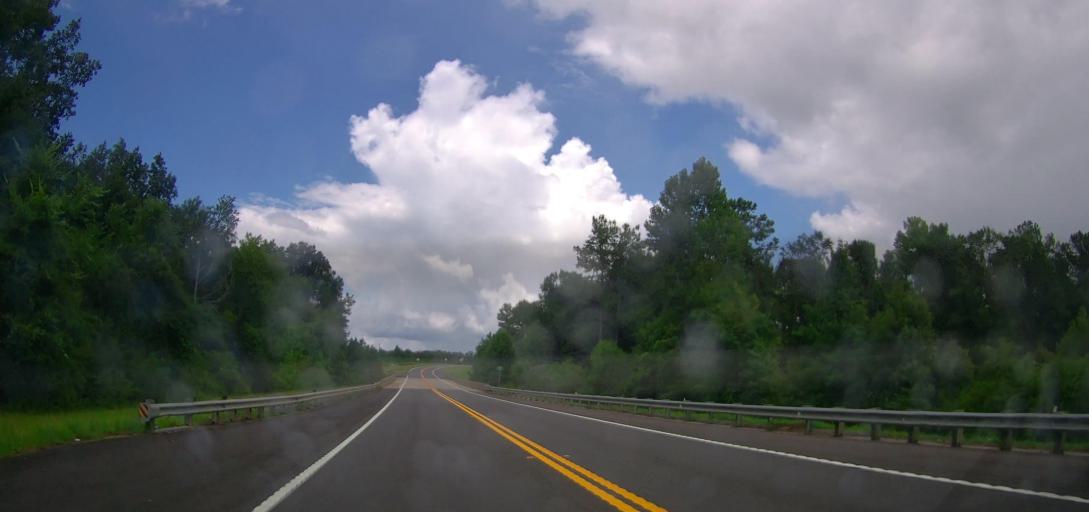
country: US
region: Georgia
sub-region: Pulaski County
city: Hawkinsville
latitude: 32.1595
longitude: -83.5471
